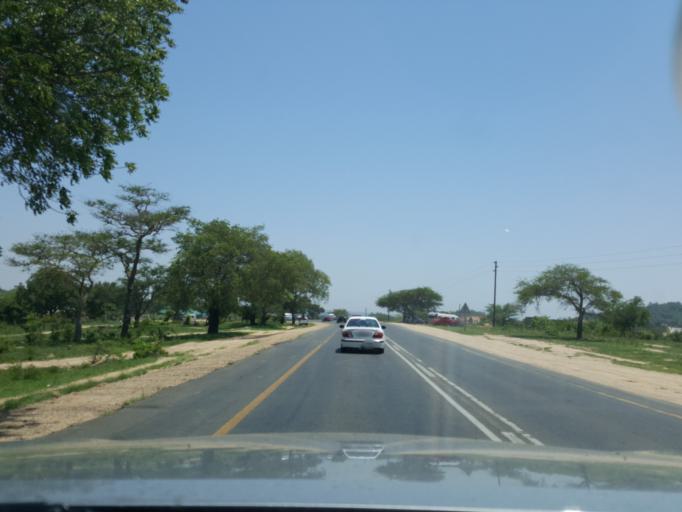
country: ZA
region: Limpopo
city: Thulamahashi
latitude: -24.8232
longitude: 31.0873
